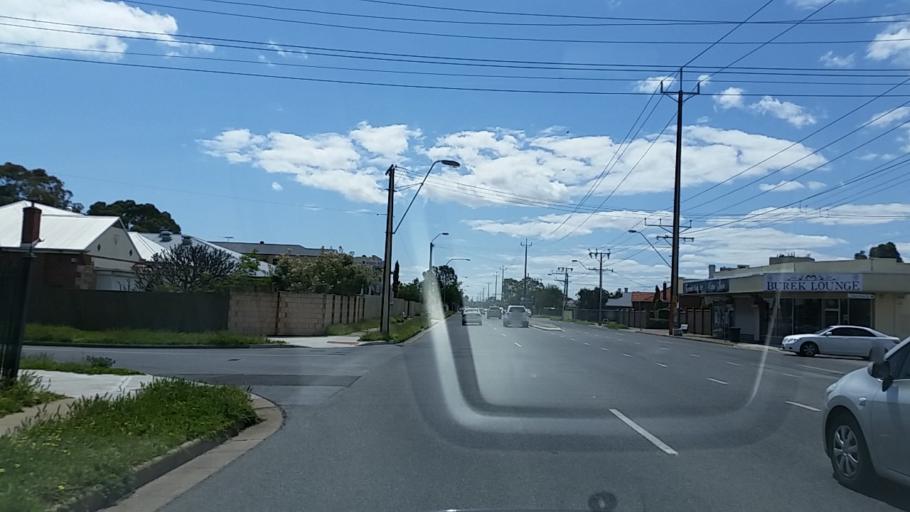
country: AU
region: South Australia
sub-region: Charles Sturt
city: Woodville West
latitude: -34.8888
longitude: 138.5313
